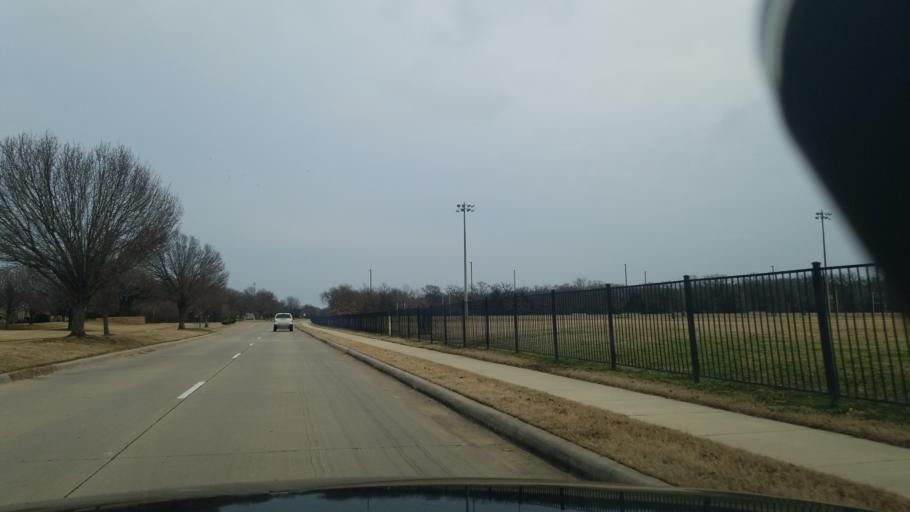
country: US
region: Texas
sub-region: Denton County
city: Corinth
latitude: 33.1534
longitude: -97.0497
